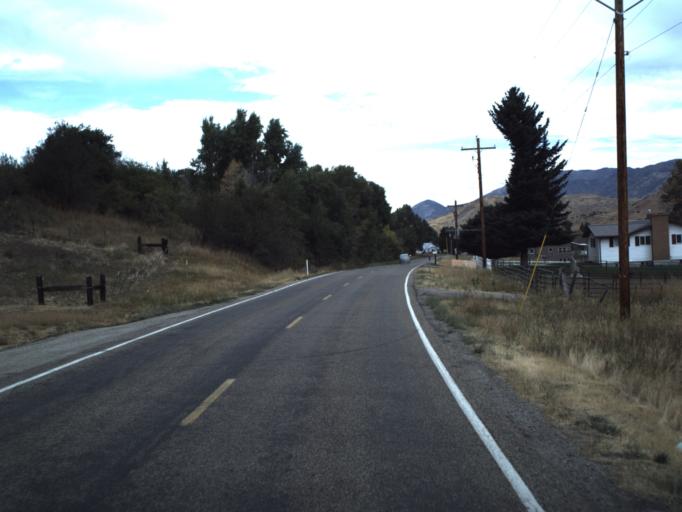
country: US
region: Utah
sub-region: Morgan County
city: Morgan
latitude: 40.9661
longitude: -111.6722
